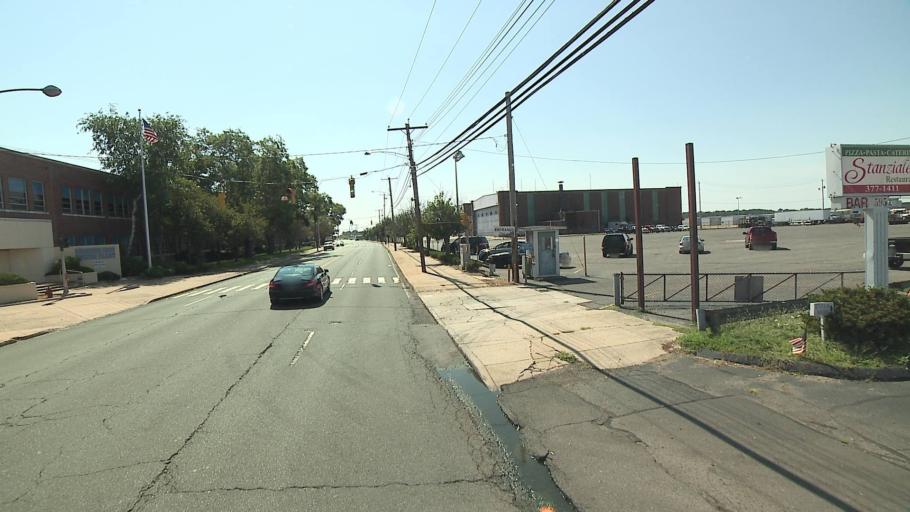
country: US
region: Connecticut
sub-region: Fairfield County
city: Stratford
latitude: 41.1701
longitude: -73.1257
